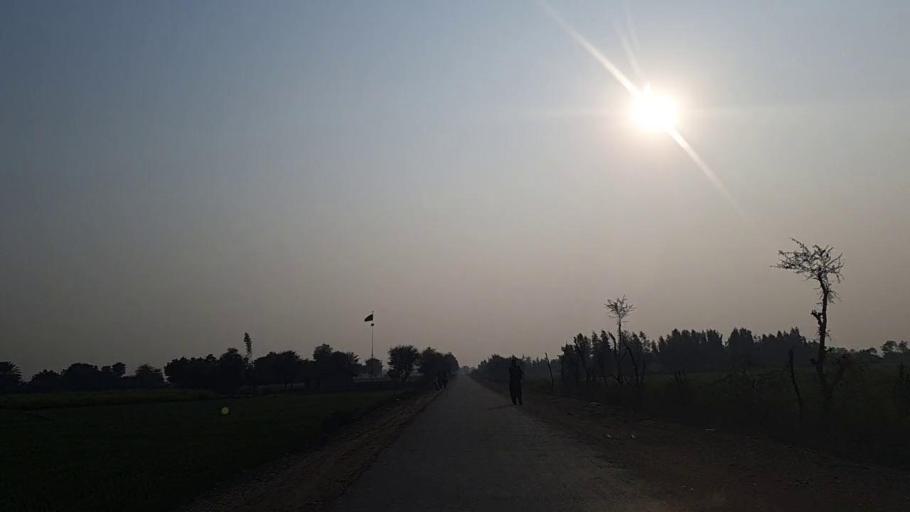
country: PK
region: Sindh
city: Nawabshah
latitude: 26.2237
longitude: 68.4784
